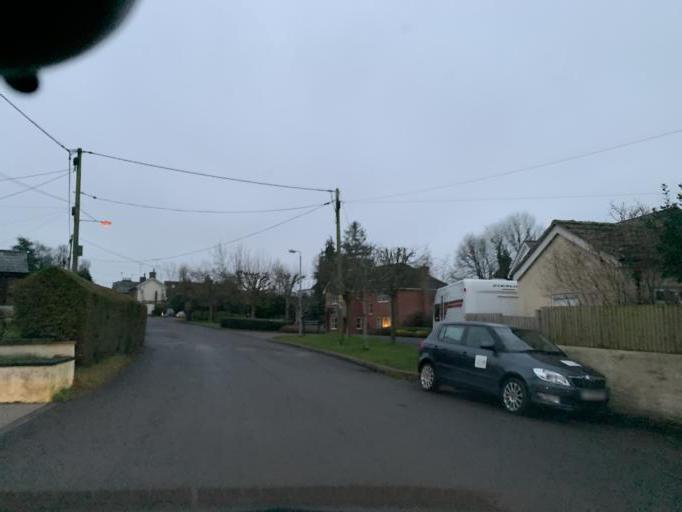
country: GB
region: England
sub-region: Wiltshire
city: Shrewton
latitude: 51.1901
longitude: -1.9029
